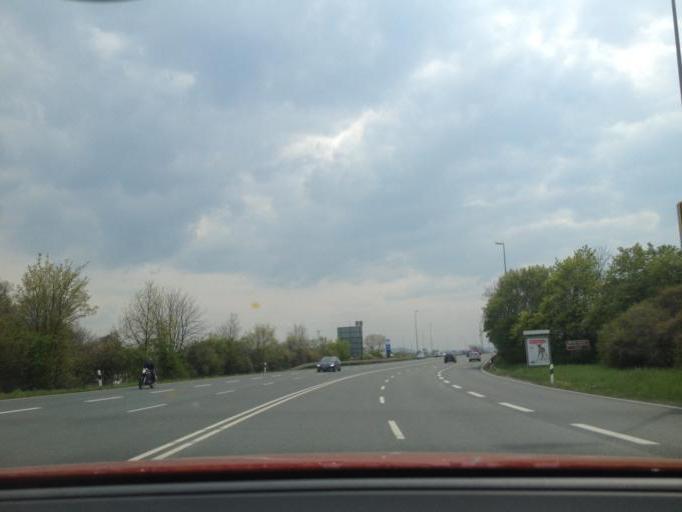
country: DE
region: Bavaria
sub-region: Upper Franconia
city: Bindlach
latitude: 49.9619
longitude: 11.6083
